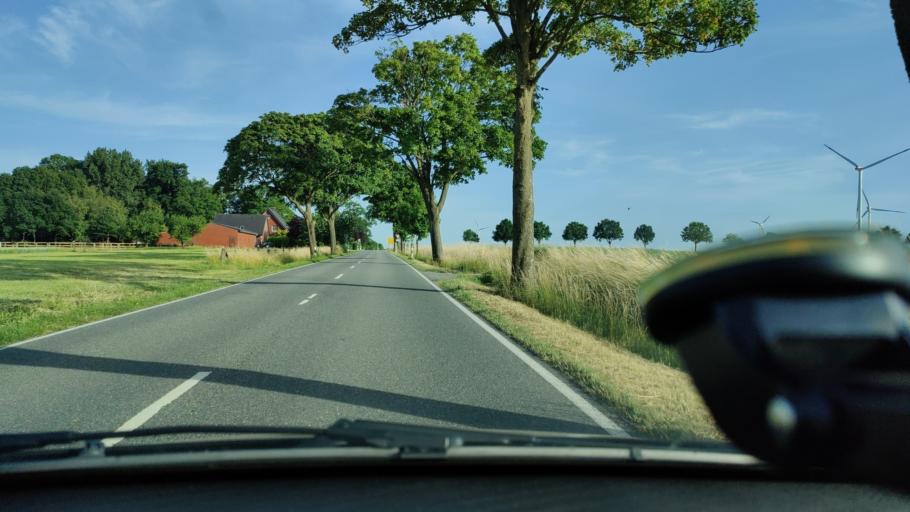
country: DE
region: North Rhine-Westphalia
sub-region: Regierungsbezirk Munster
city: Coesfeld
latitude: 52.0208
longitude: 7.1813
